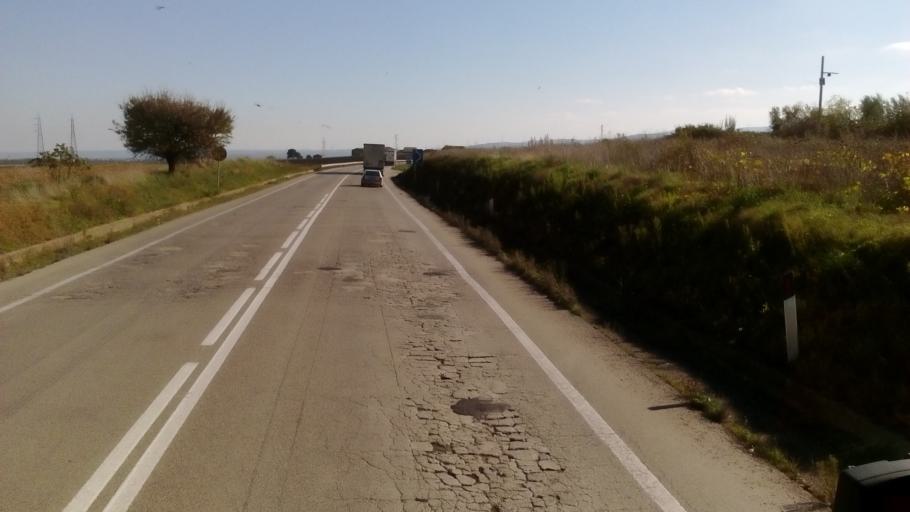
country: IT
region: Apulia
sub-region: Provincia di Foggia
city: Candela
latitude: 41.1187
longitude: 15.5753
